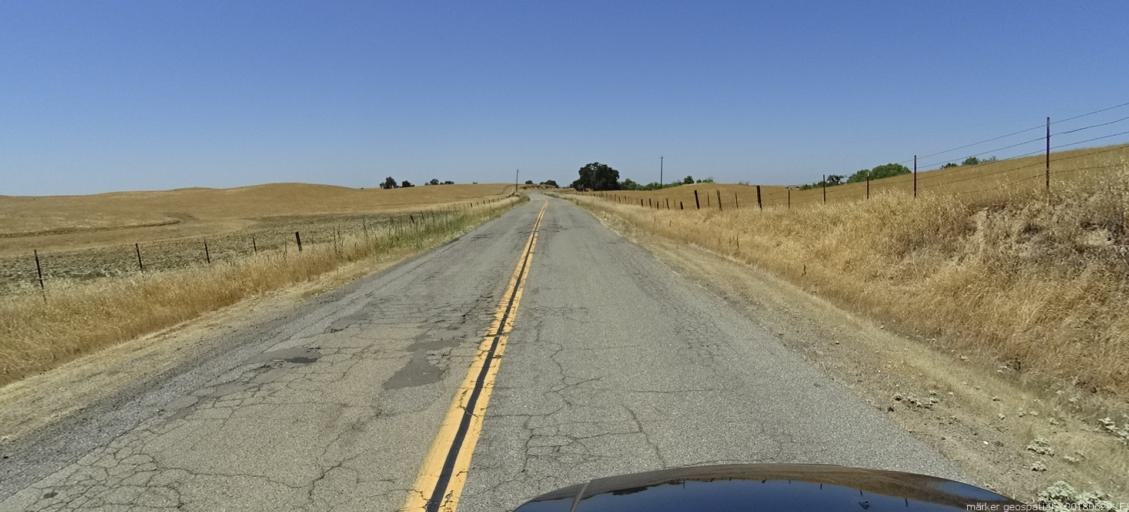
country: US
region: California
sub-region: Madera County
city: Bonadelle Ranchos-Madera Ranchos
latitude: 37.0782
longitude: -119.8970
